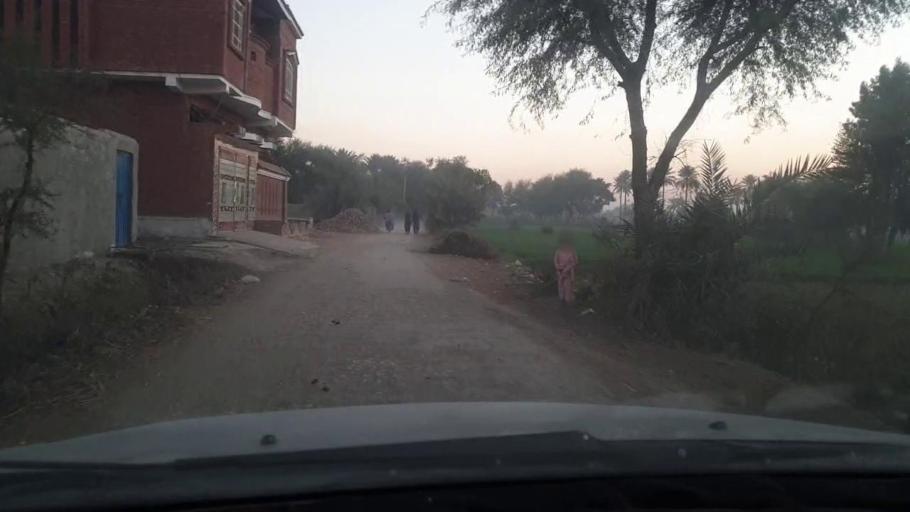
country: PK
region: Sindh
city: Ghotki
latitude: 28.0070
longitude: 69.3379
